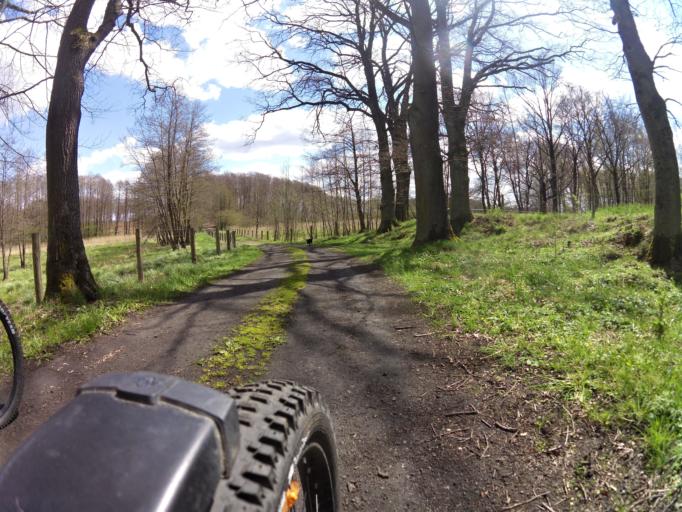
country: PL
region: West Pomeranian Voivodeship
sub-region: Powiat gryficki
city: Gryfice
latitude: 53.8448
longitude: 15.1761
